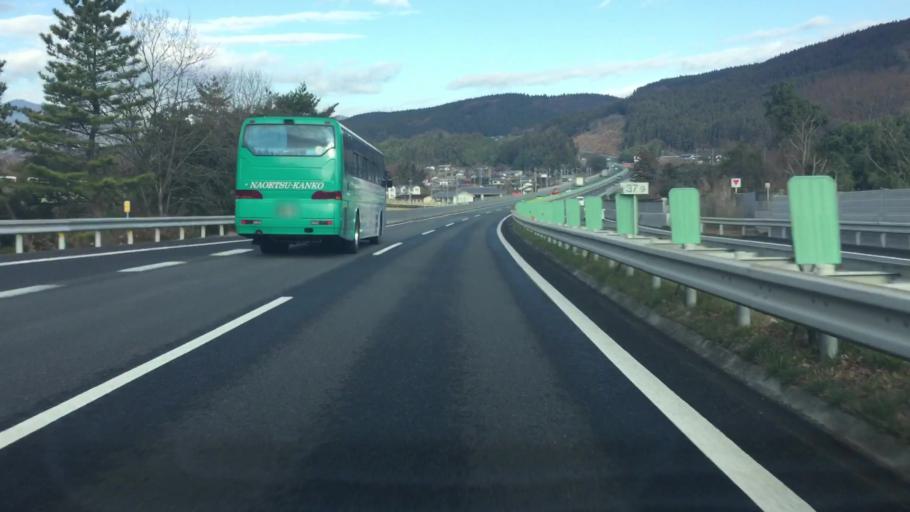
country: JP
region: Gunma
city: Annaka
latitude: 36.3159
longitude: 138.7734
